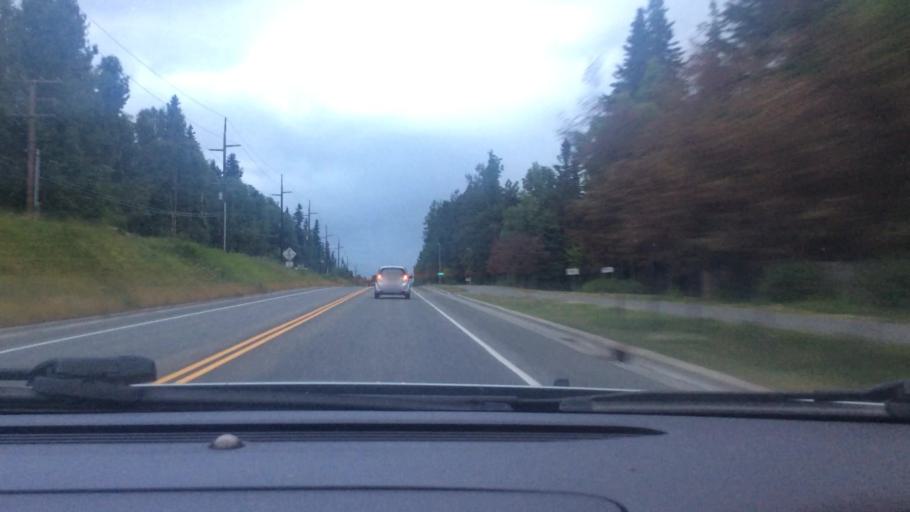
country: US
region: Alaska
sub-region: Anchorage Municipality
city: Anchorage
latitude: 61.1427
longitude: -149.8042
